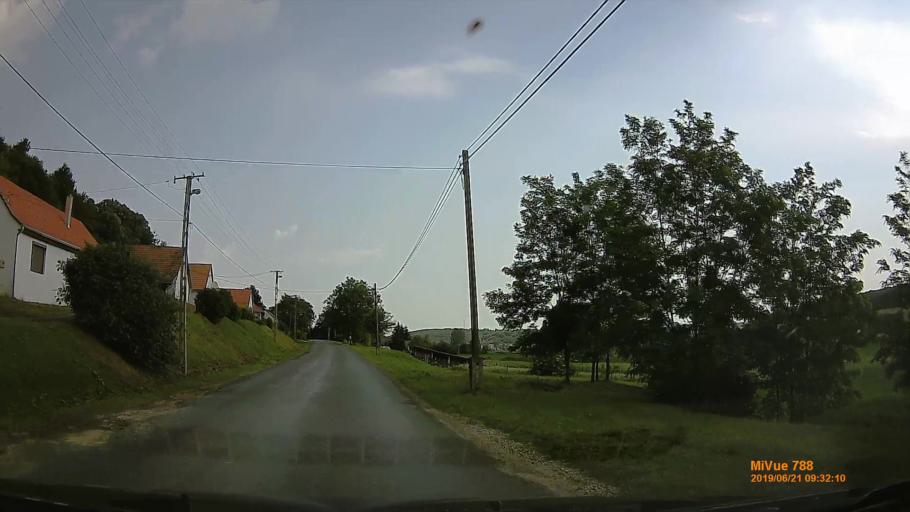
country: HU
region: Somogy
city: Taszar
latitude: 46.3101
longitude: 17.8829
